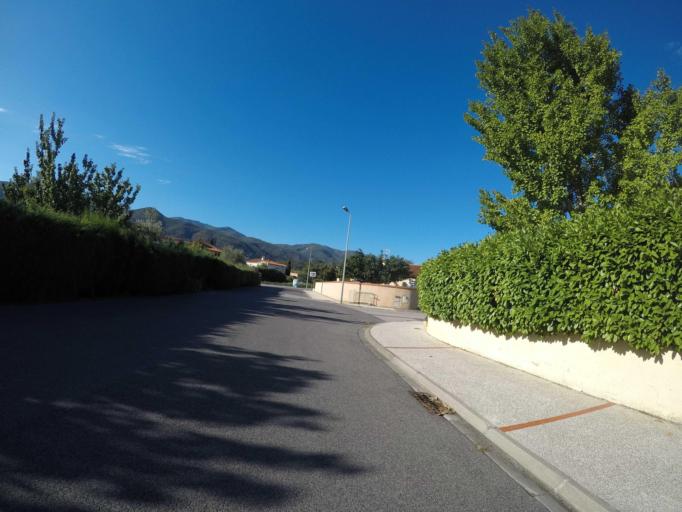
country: FR
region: Languedoc-Roussillon
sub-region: Departement des Pyrenees-Orientales
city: Ceret
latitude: 42.4988
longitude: 2.7467
